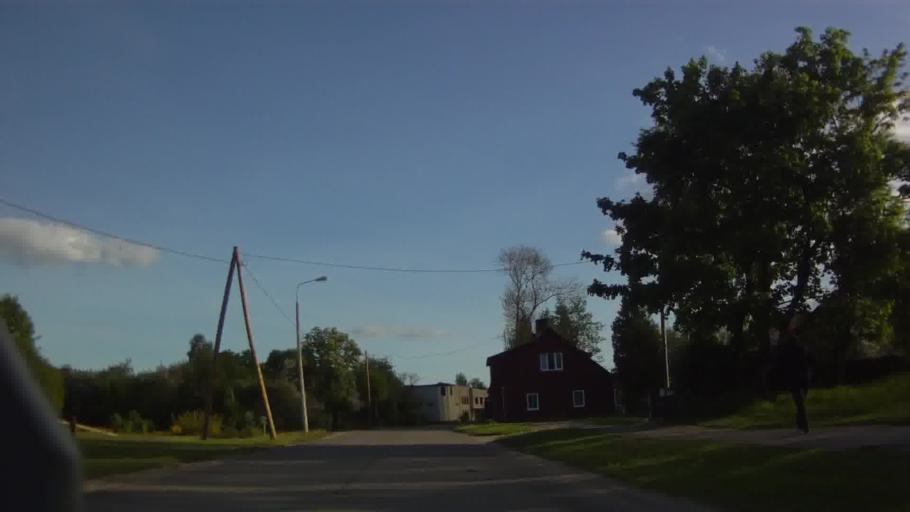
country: LV
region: Baldone
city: Baldone
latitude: 56.7450
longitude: 24.3965
